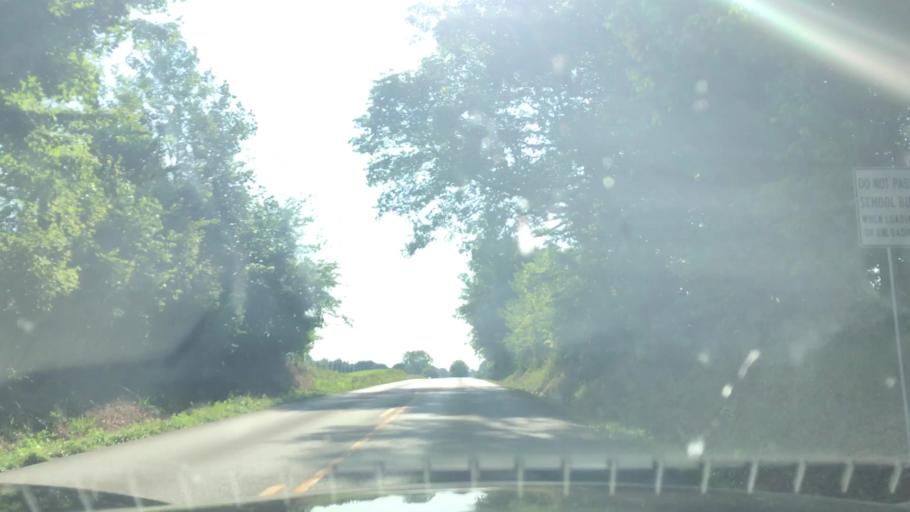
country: US
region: Kentucky
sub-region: Hart County
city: Horse Cave
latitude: 37.1665
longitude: -85.8358
